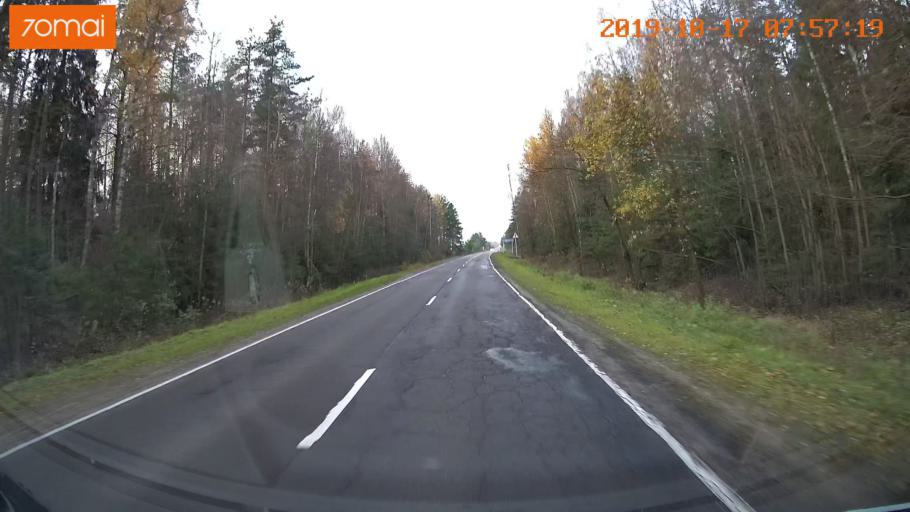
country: RU
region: Vladimir
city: Bavleny
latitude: 56.4129
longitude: 39.5786
